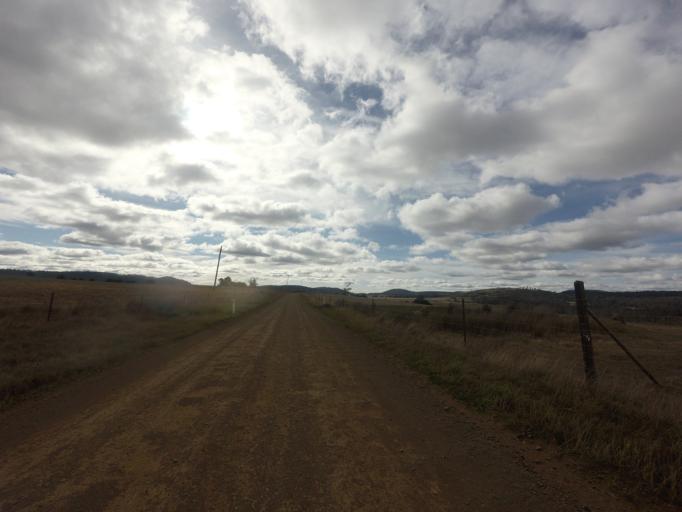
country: AU
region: Tasmania
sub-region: Brighton
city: Bridgewater
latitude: -42.4338
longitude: 147.3859
